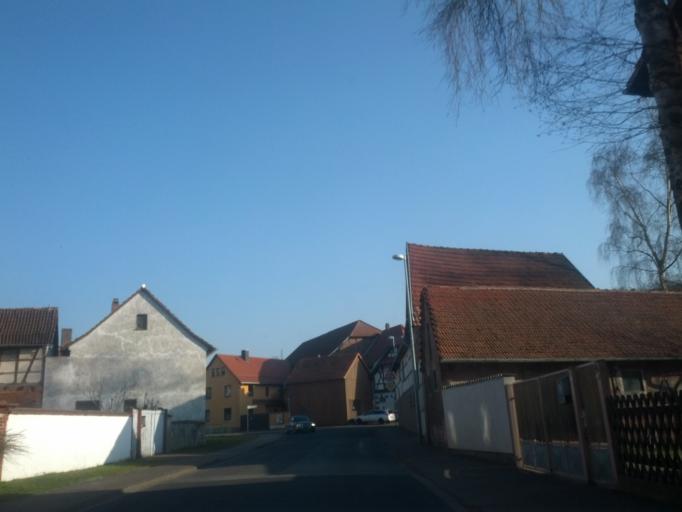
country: DE
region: Thuringia
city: Bischofroda
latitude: 51.0443
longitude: 10.3839
